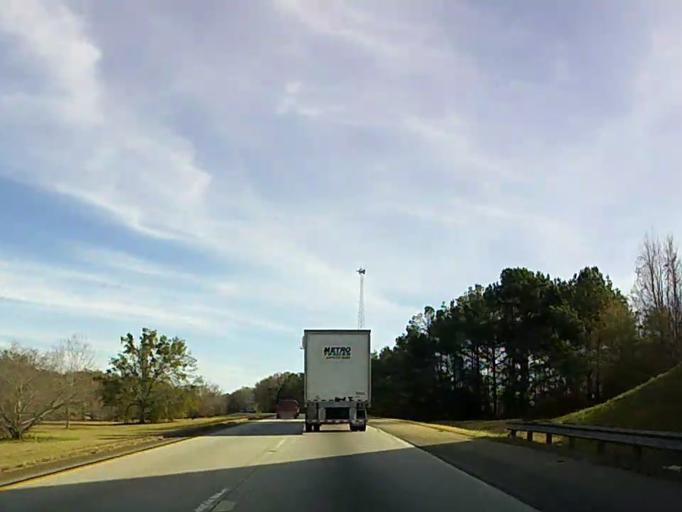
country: US
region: Georgia
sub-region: Monroe County
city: Forsyth
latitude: 32.9563
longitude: -83.8114
